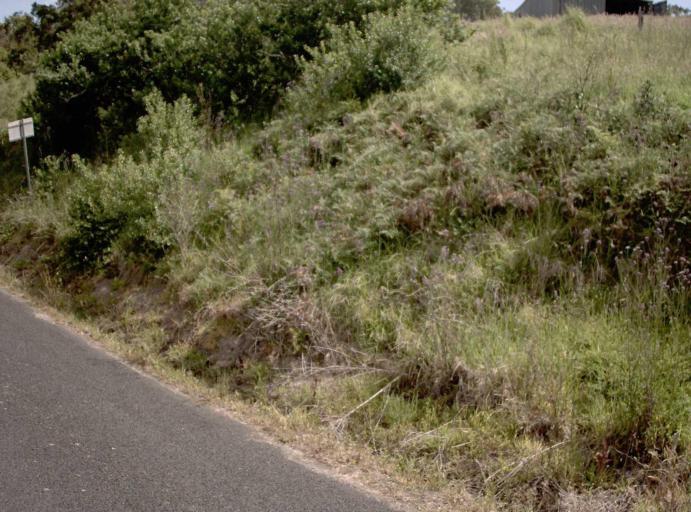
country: AU
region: New South Wales
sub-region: Bega Valley
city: Eden
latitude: -37.4765
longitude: 149.5958
